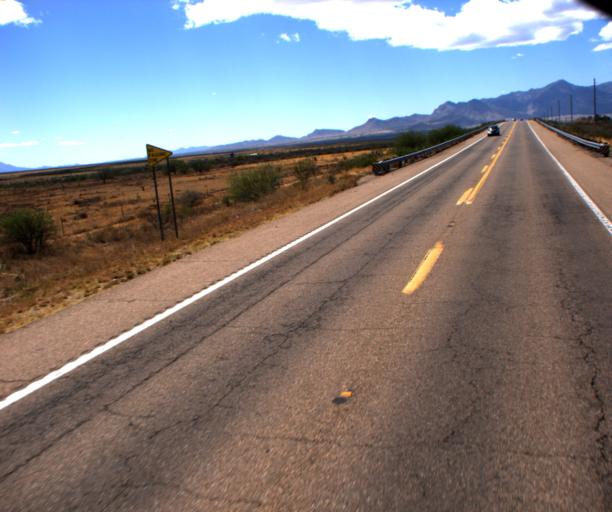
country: US
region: Arizona
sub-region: Cochise County
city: Naco
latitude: 31.3800
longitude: -110.0441
